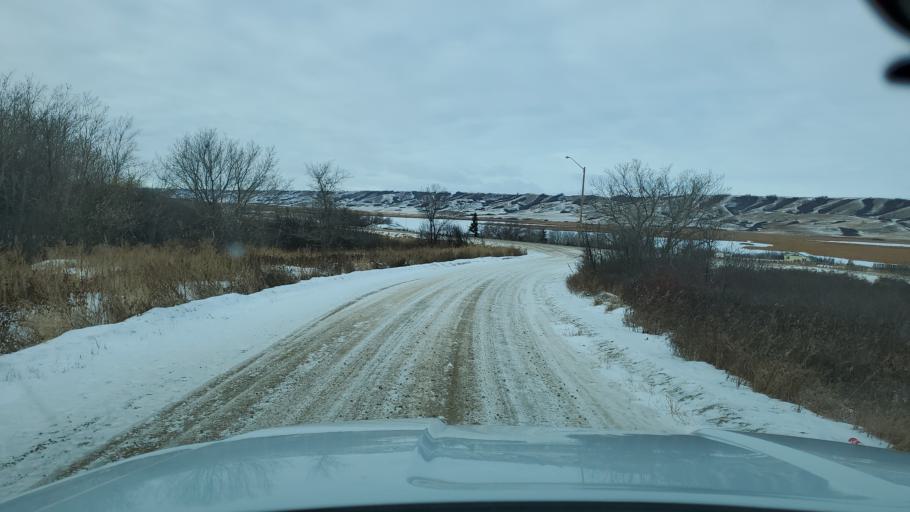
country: CA
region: Saskatchewan
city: White City
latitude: 50.7805
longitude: -104.1422
